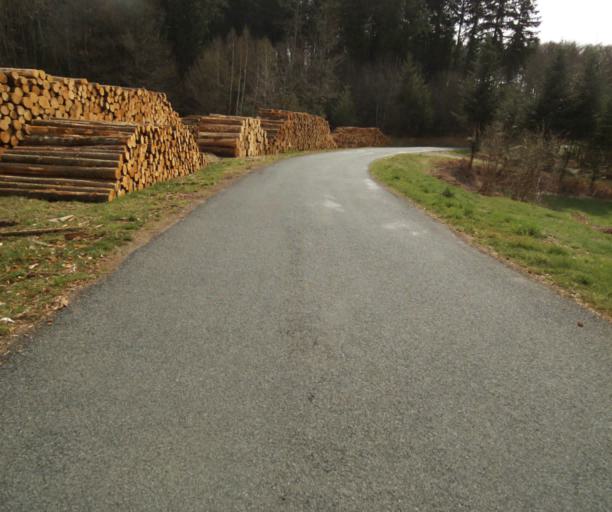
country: FR
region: Limousin
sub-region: Departement de la Correze
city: Correze
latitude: 45.3751
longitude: 1.9014
